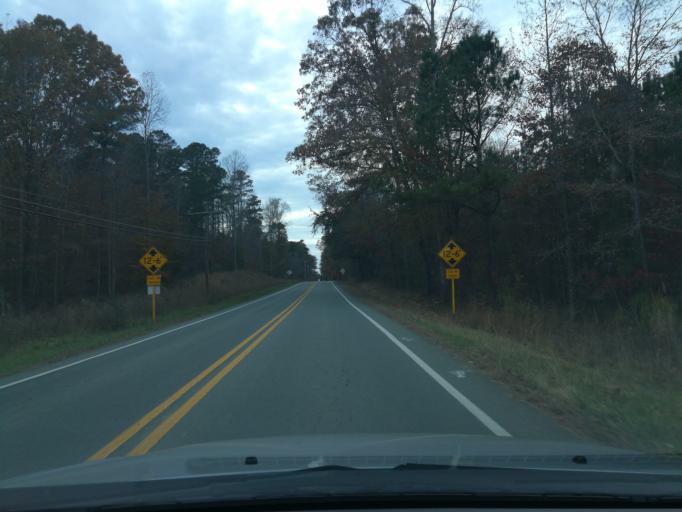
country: US
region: North Carolina
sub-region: Orange County
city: Hillsborough
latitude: 36.0316
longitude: -79.0225
